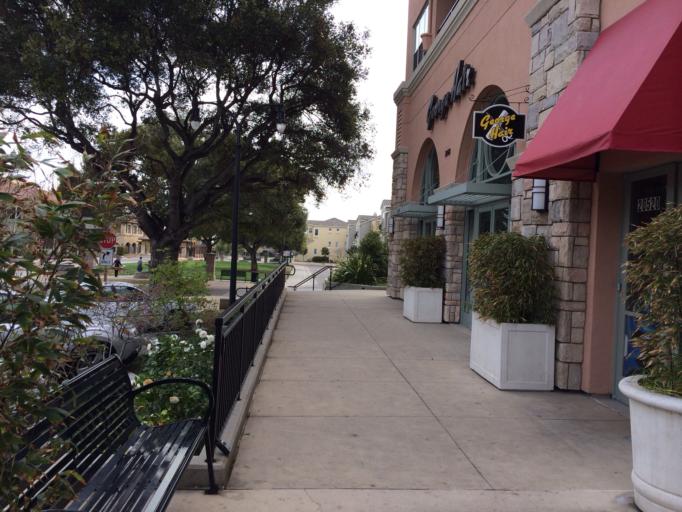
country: US
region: California
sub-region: Santa Clara County
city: Cupertino
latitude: 37.3184
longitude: -122.0312
